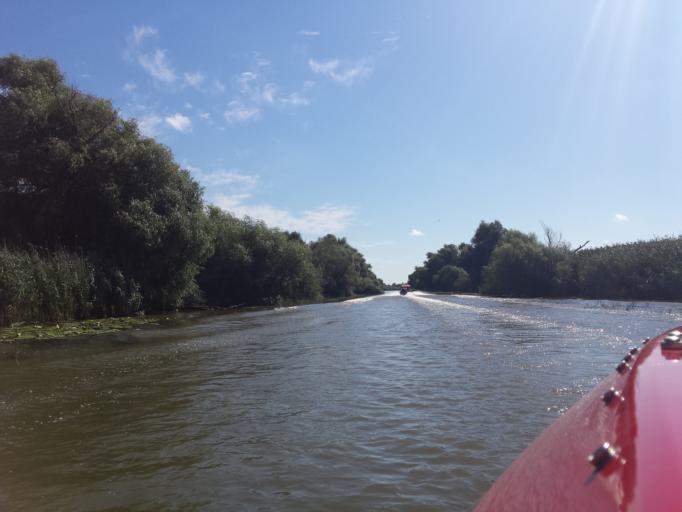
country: RO
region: Tulcea
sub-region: Comuna Mahmudia
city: Mahmudia
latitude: 45.2388
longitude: 29.1295
